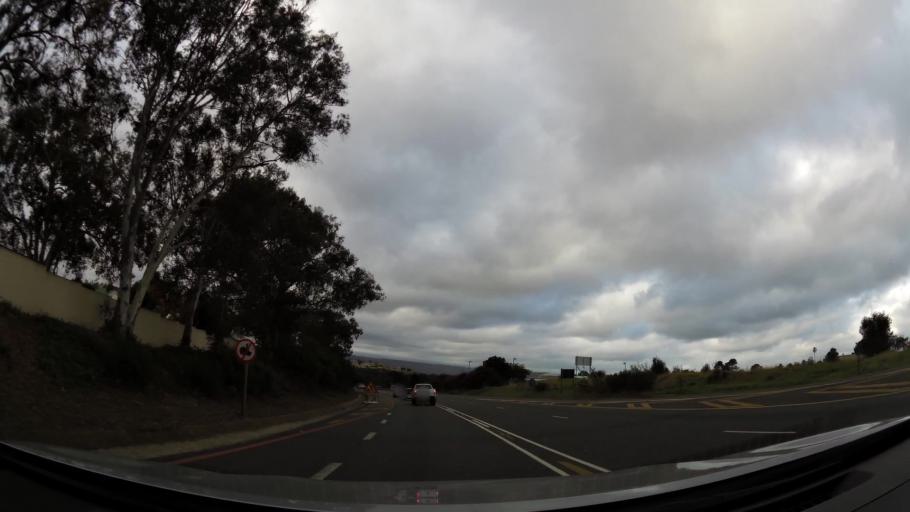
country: ZA
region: Western Cape
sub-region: Eden District Municipality
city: Plettenberg Bay
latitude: -34.0486
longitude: 23.3598
